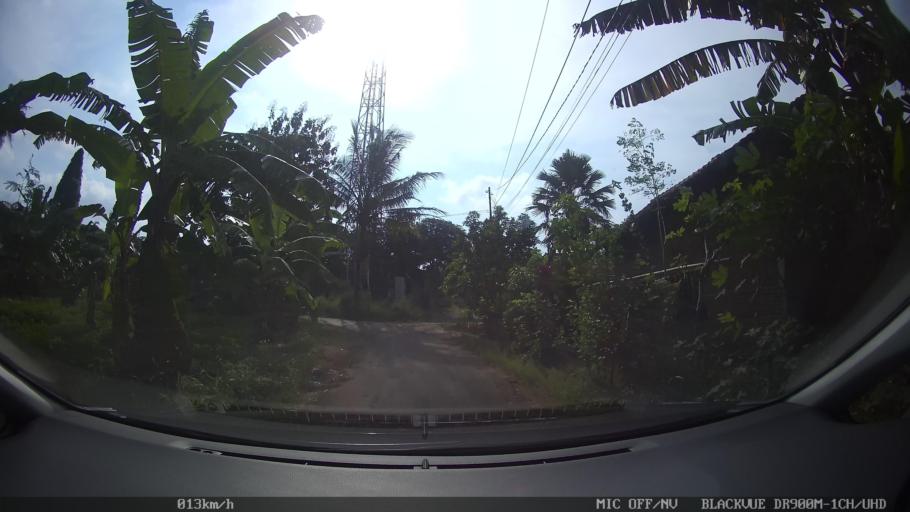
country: ID
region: Lampung
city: Kedaton
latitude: -5.3860
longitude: 105.2241
